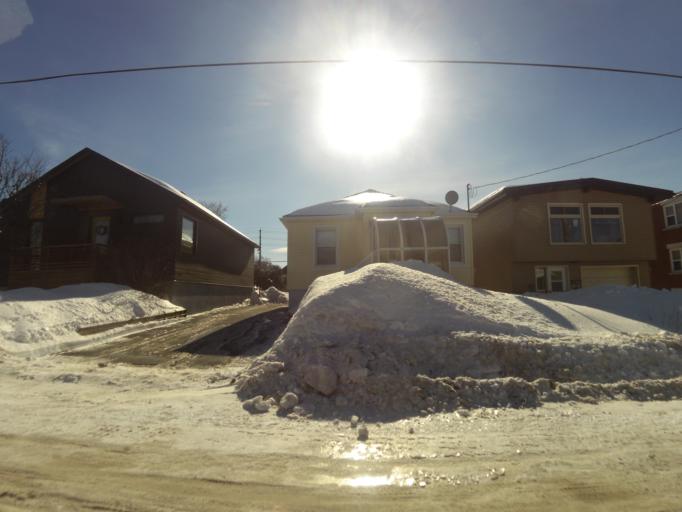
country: CA
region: Ontario
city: Ottawa
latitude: 45.4398
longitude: -75.6584
